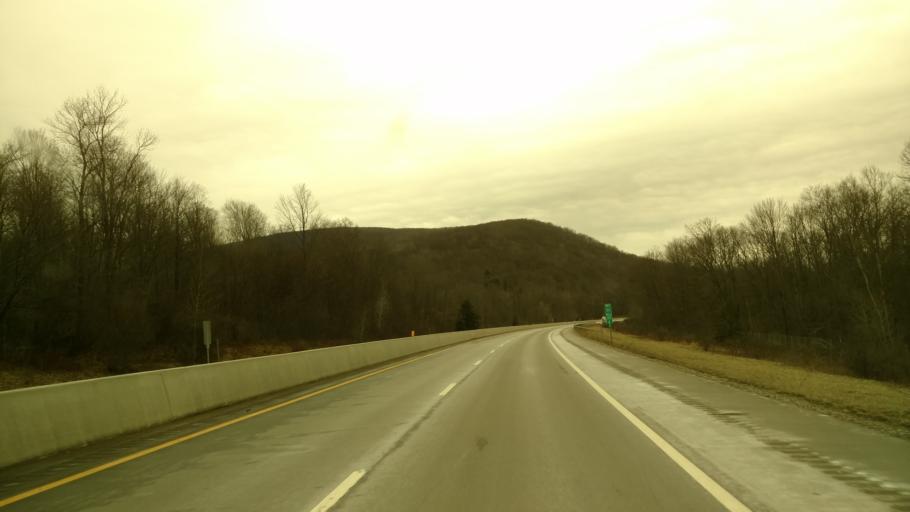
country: US
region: New York
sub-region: Cattaraugus County
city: Salamanca
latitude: 42.1021
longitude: -78.6612
